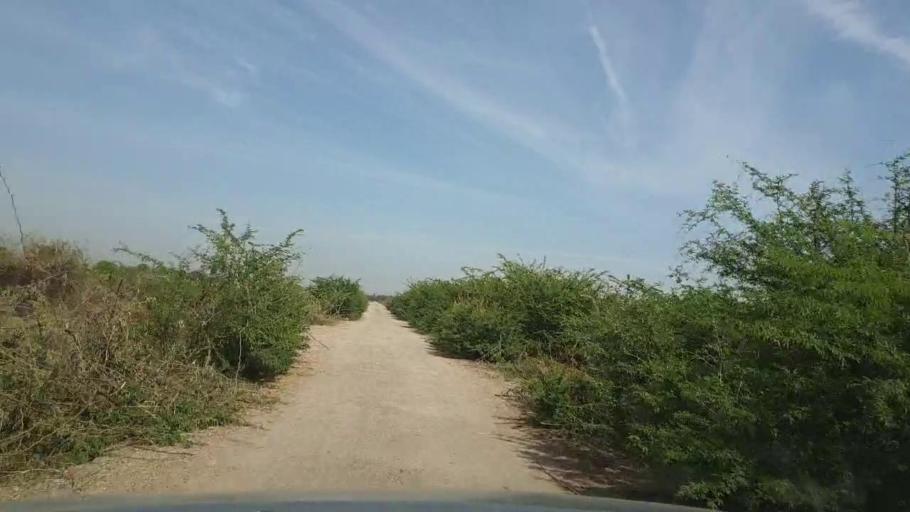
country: PK
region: Sindh
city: Nabisar
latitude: 25.1287
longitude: 69.6400
